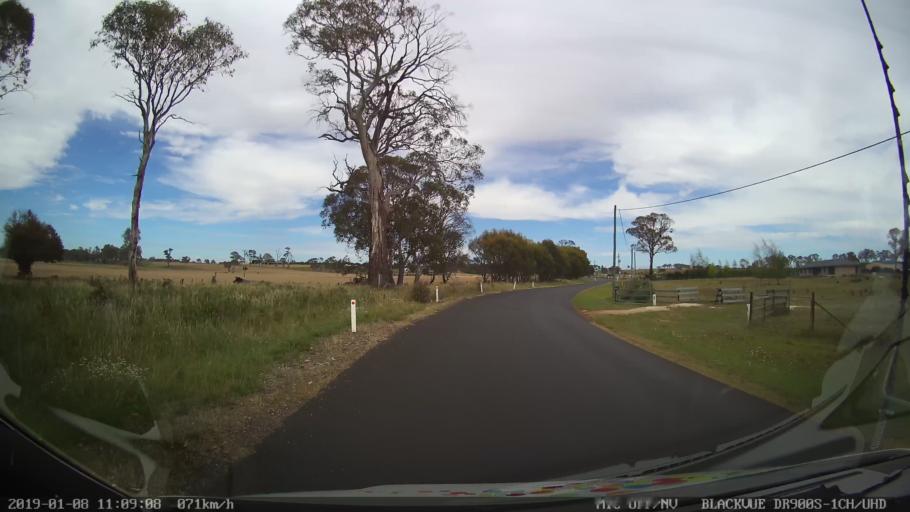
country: AU
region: New South Wales
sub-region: Guyra
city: Guyra
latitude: -30.2246
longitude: 151.6508
